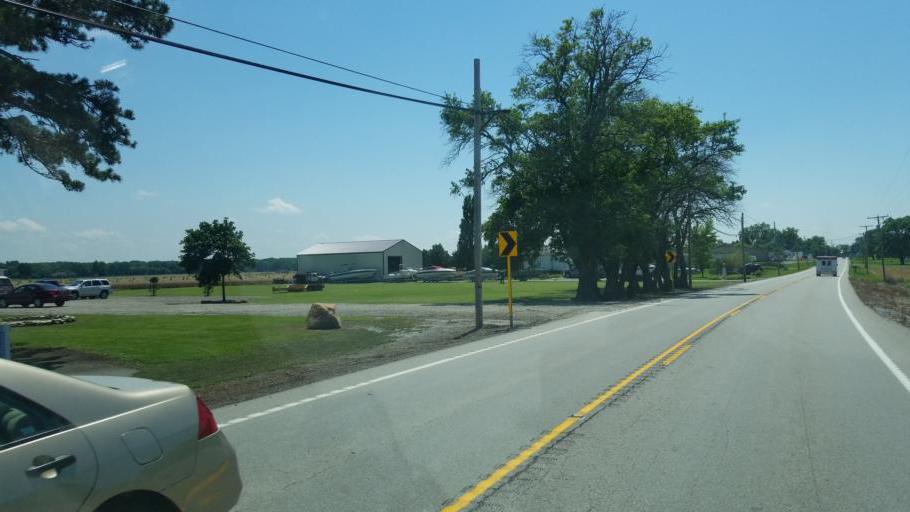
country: US
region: Ohio
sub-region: Erie County
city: Sandusky
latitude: 41.4396
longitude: -82.8184
